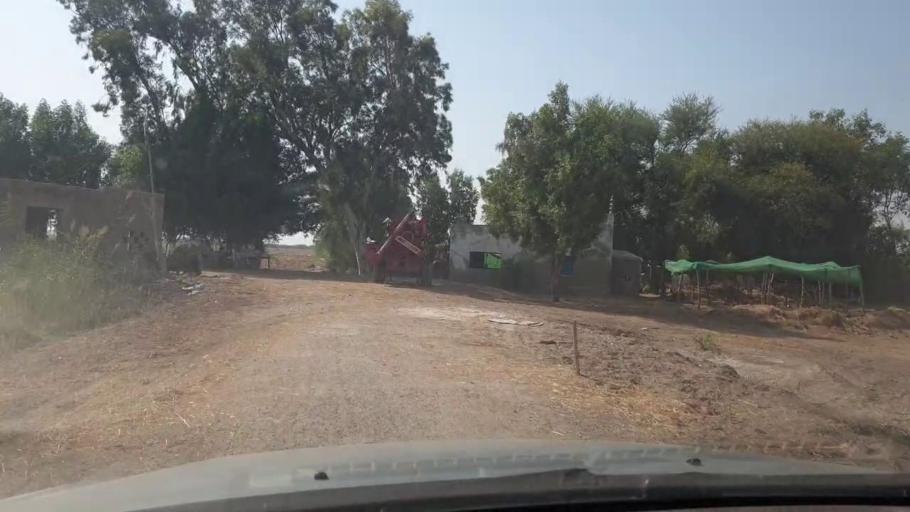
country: PK
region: Sindh
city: Bulri
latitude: 24.8996
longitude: 68.4175
